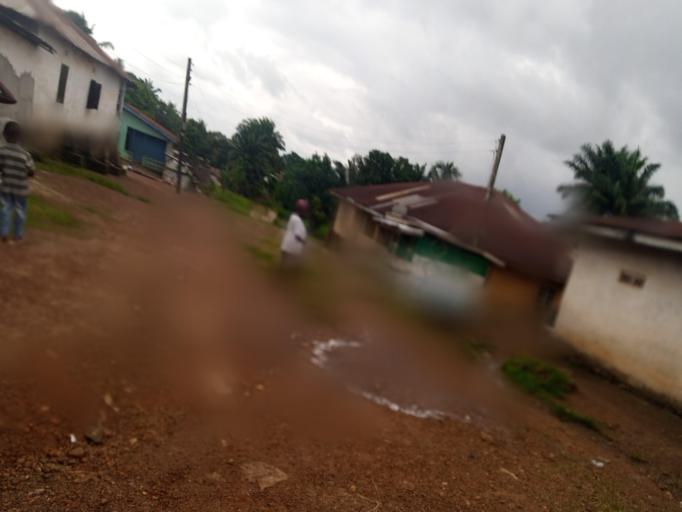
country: SL
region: Eastern Province
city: Kenema
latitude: 7.8613
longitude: -11.1948
